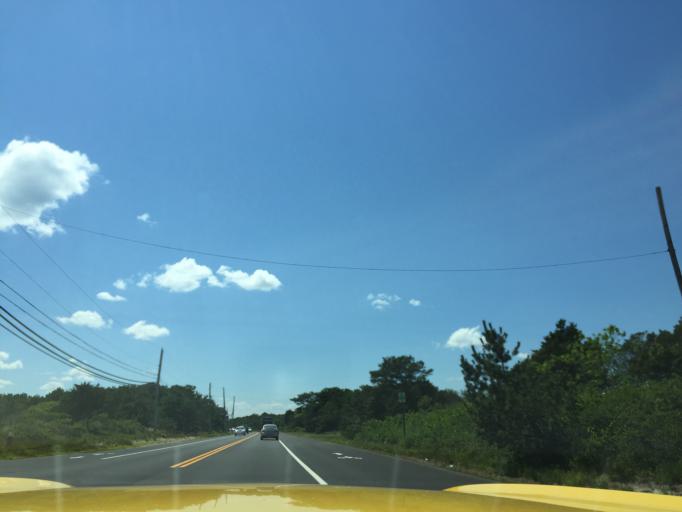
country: US
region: New York
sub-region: Suffolk County
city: Amagansett
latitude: 40.9949
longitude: -72.0574
